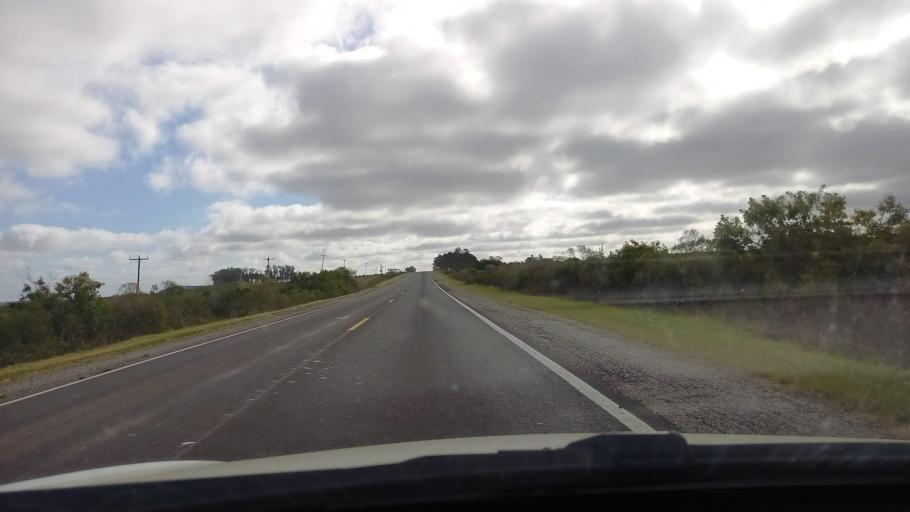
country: BR
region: Rio Grande do Sul
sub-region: Dom Pedrito
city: Dom Pedrito
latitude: -30.9046
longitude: -54.8258
